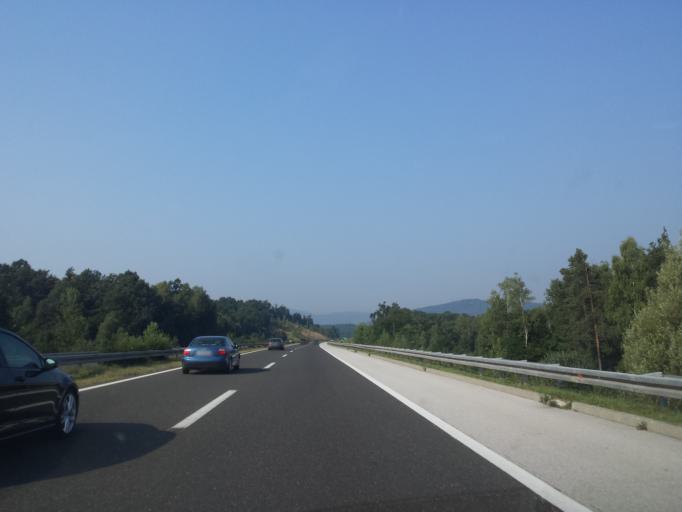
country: SI
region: Crnomelj
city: Crnomelj
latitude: 45.4341
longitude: 15.3256
